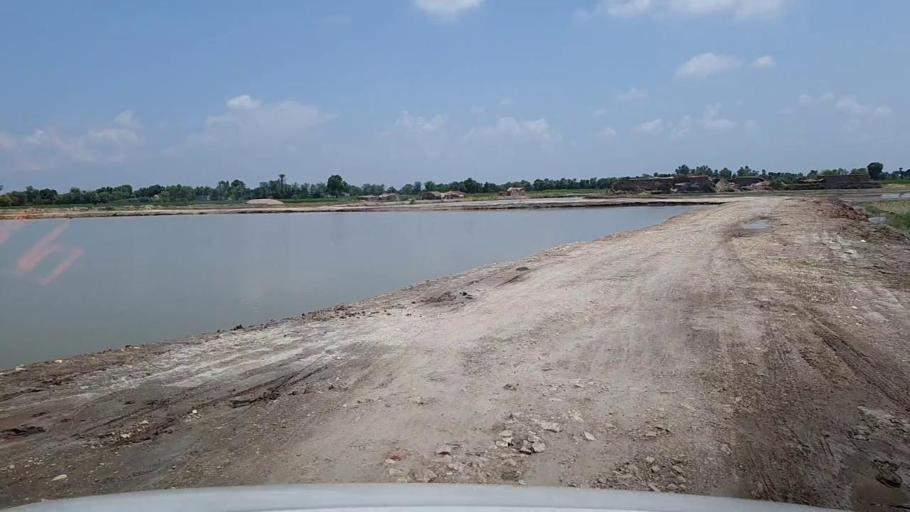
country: PK
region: Sindh
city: Kandiaro
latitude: 26.9862
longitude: 68.2346
